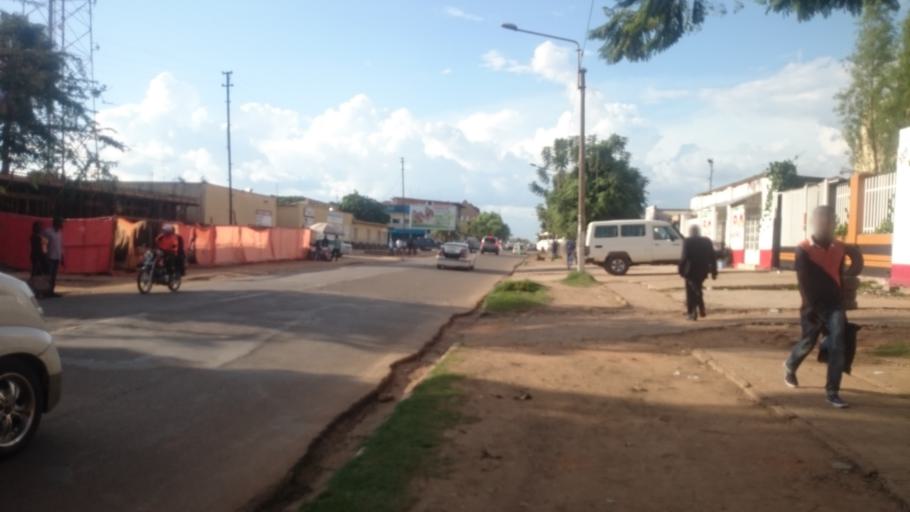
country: CD
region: Katanga
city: Lubumbashi
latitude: -11.6713
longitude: 27.4820
